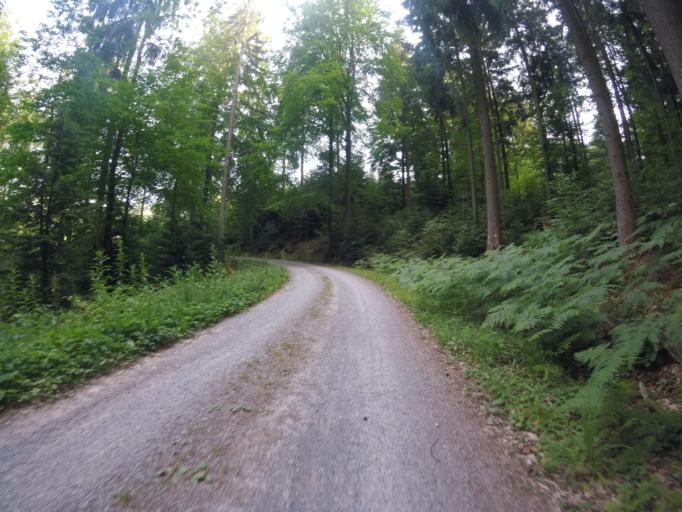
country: DE
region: Baden-Wuerttemberg
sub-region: Regierungsbezirk Stuttgart
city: Sulzbach an der Murr
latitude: 48.9743
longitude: 9.5087
